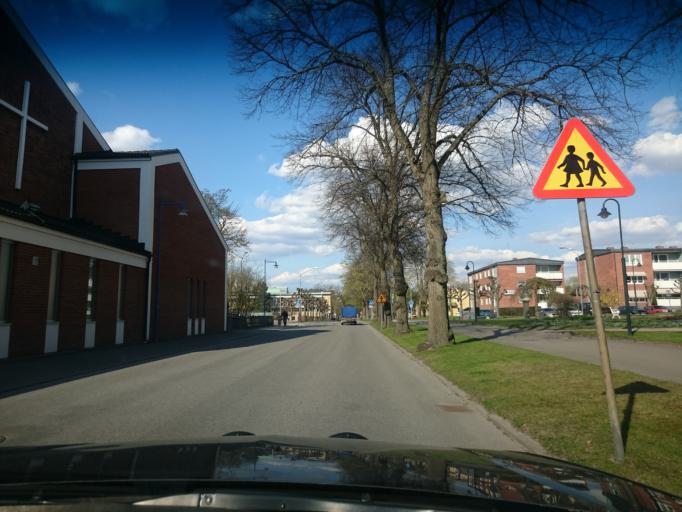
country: SE
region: Joenkoeping
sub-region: Vetlanda Kommun
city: Vetlanda
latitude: 57.4282
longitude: 15.0815
